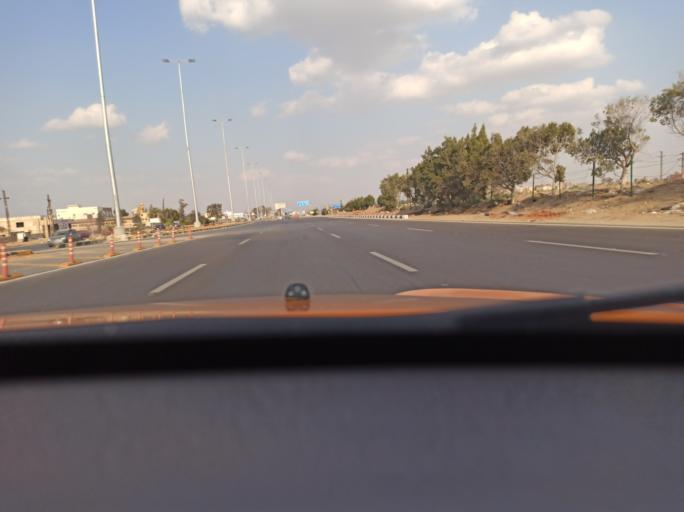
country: EG
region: Al Isma'iliyah
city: Ismailia
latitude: 30.6185
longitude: 32.2353
